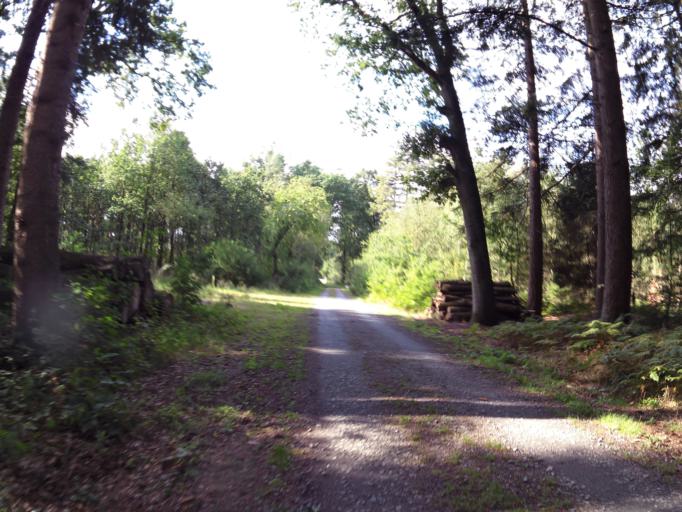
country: DE
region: Lower Saxony
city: Bremervorde
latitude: 53.4715
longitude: 9.1454
